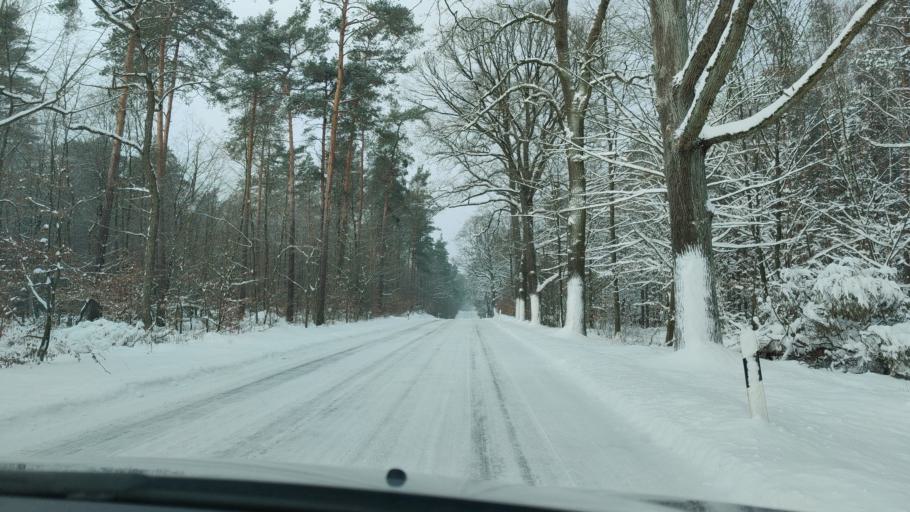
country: DE
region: Saxony
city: Bad Duben
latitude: 51.6514
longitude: 12.6022
